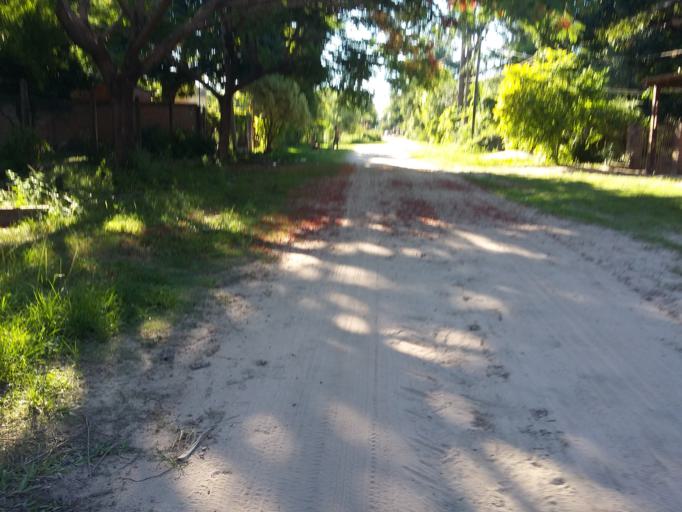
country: AR
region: Corrientes
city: San Luis del Palmar
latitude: -27.4554
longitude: -58.6508
